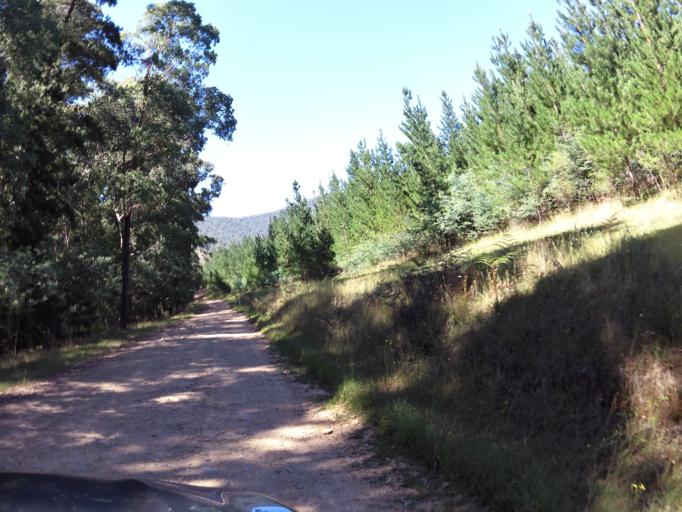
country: AU
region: Victoria
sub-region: Alpine
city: Mount Beauty
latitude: -36.7503
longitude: 146.9548
